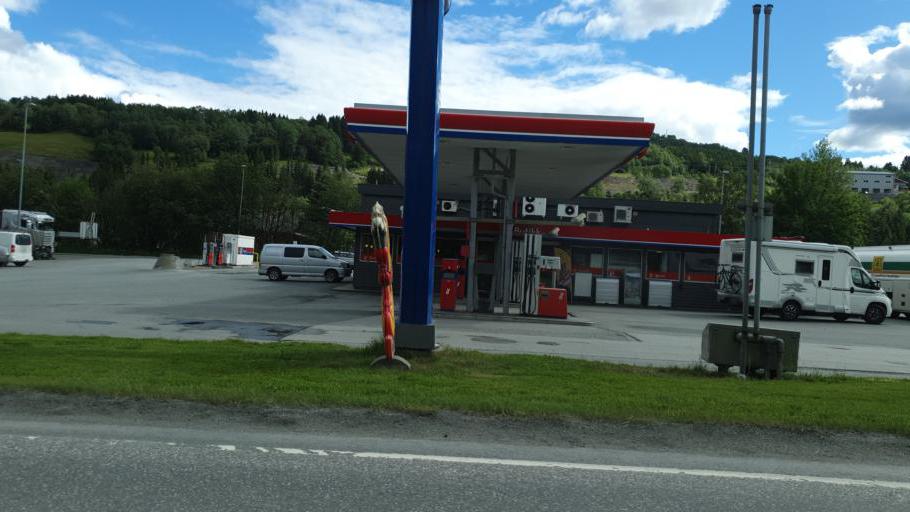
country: NO
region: Sor-Trondelag
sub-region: Midtre Gauldal
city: Storen
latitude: 62.9482
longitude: 10.1896
